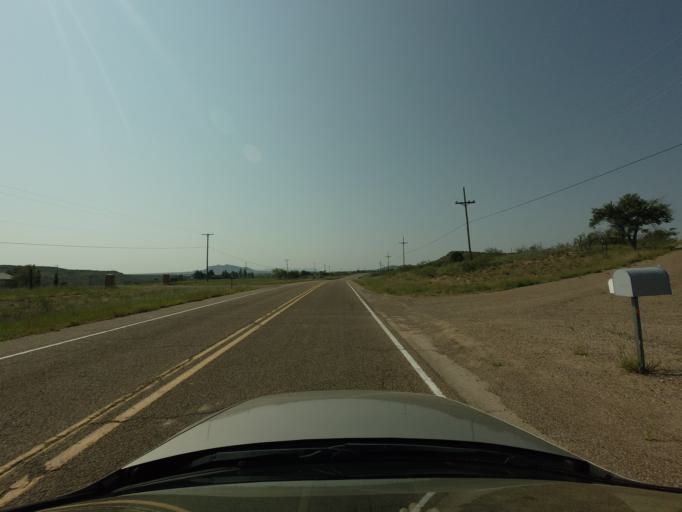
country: US
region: New Mexico
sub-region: Quay County
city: Tucumcari
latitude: 35.1382
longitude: -103.7251
